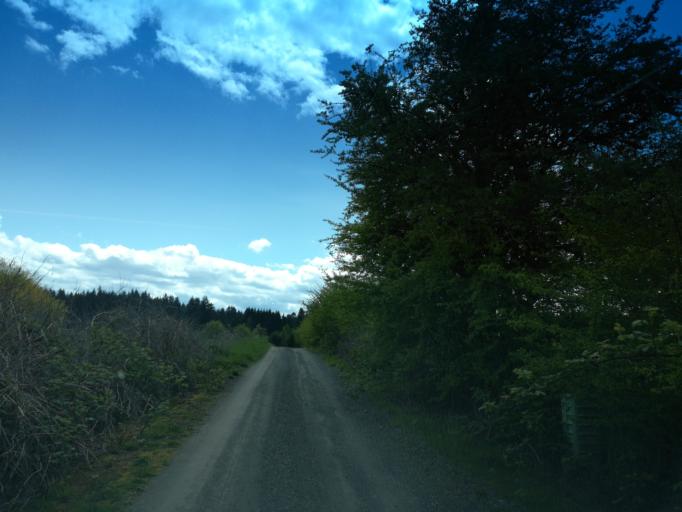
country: US
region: Oregon
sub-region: Clackamas County
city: Damascus
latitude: 45.4528
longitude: -122.4476
